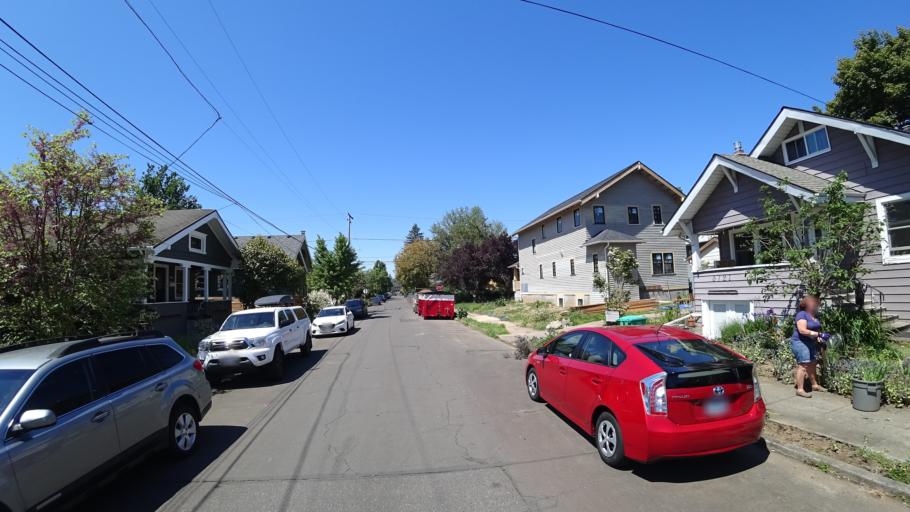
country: US
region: Oregon
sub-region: Multnomah County
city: Portland
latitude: 45.5067
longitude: -122.6251
